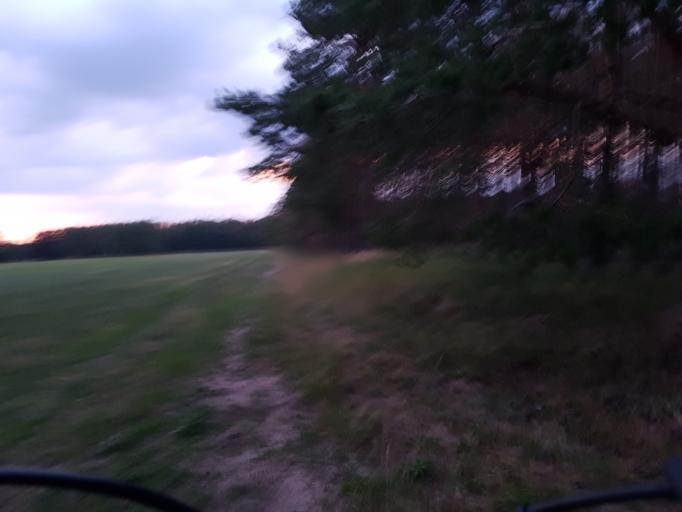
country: DE
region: Brandenburg
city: Schilda
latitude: 51.5577
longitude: 13.3678
